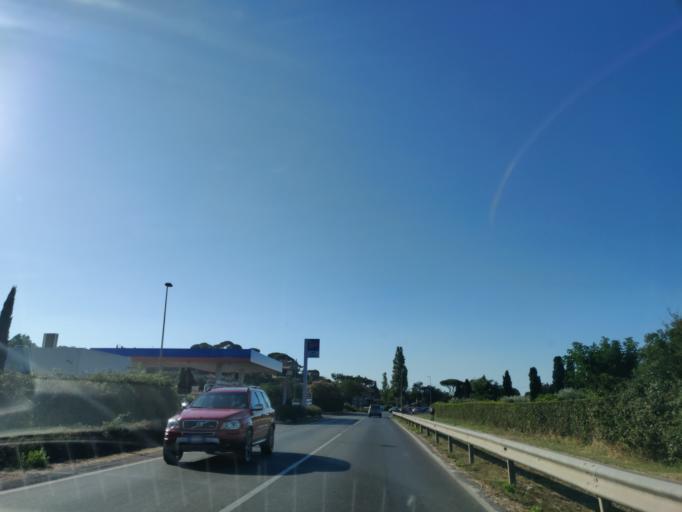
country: IT
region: Tuscany
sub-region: Provincia di Grosseto
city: Porto Ercole
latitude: 42.4253
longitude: 11.1985
